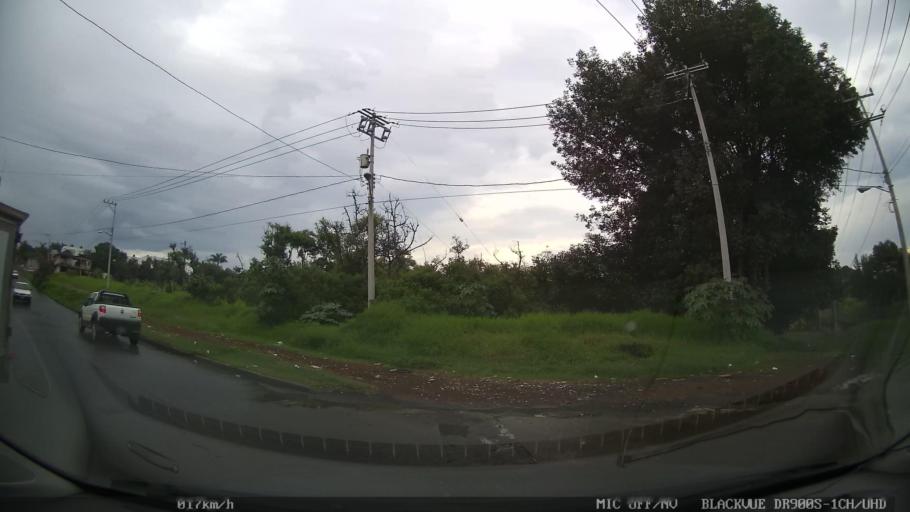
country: MX
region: Michoacan
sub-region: Uruapan
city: Santa Rosa (Santa Barbara)
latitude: 19.3878
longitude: -102.0480
